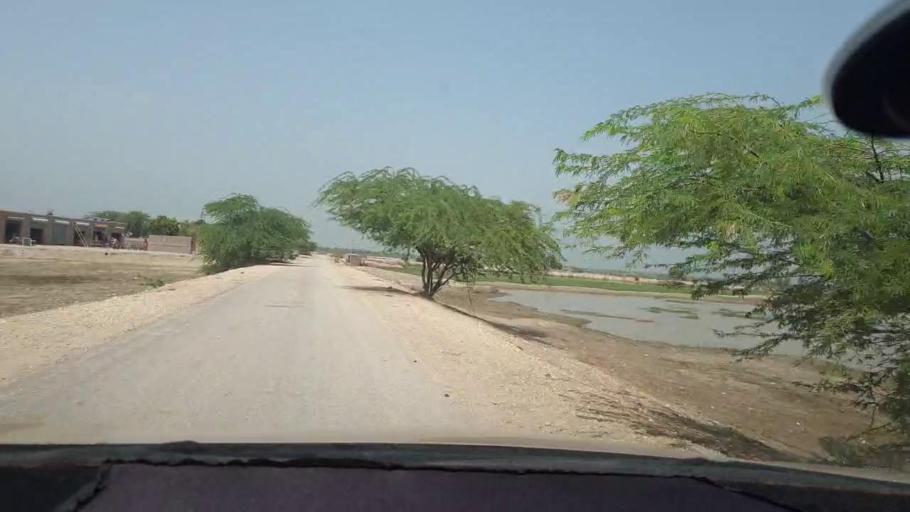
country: PK
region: Sindh
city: Kambar
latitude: 27.6750
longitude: 67.9111
